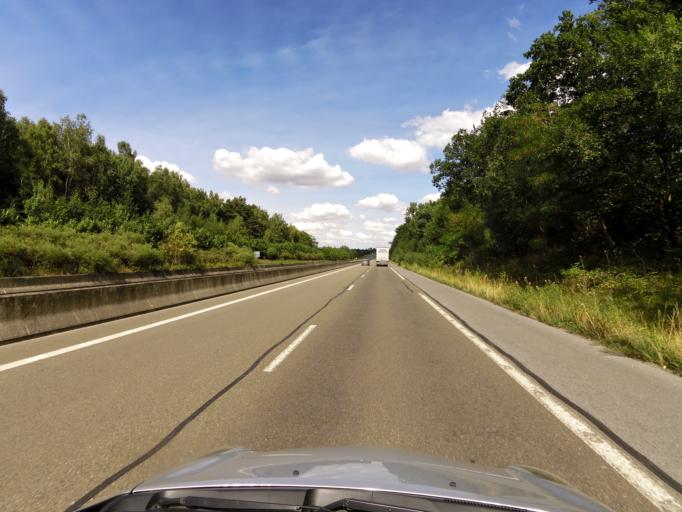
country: FR
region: Picardie
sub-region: Departement de l'Aisne
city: Laon
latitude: 49.5040
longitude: 3.5651
